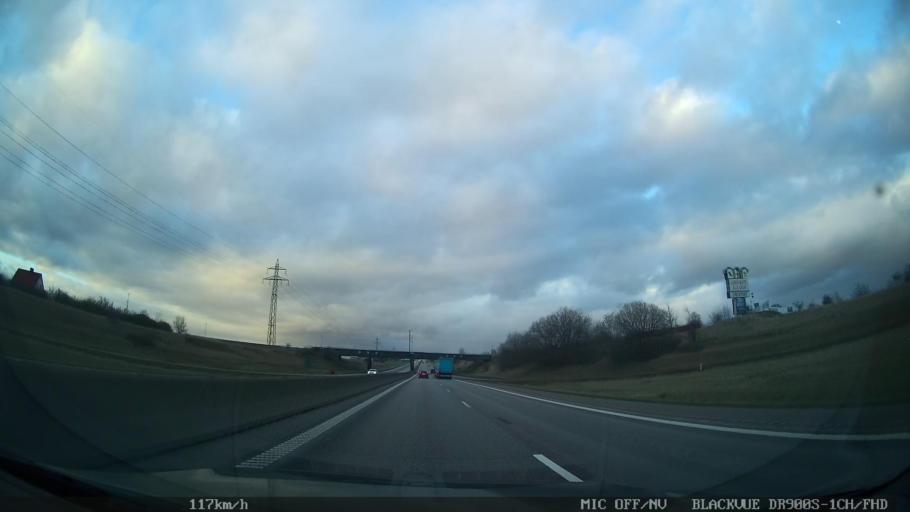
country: SE
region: Skane
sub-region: Astorps Kommun
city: Astorp
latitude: 56.1278
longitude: 12.9136
